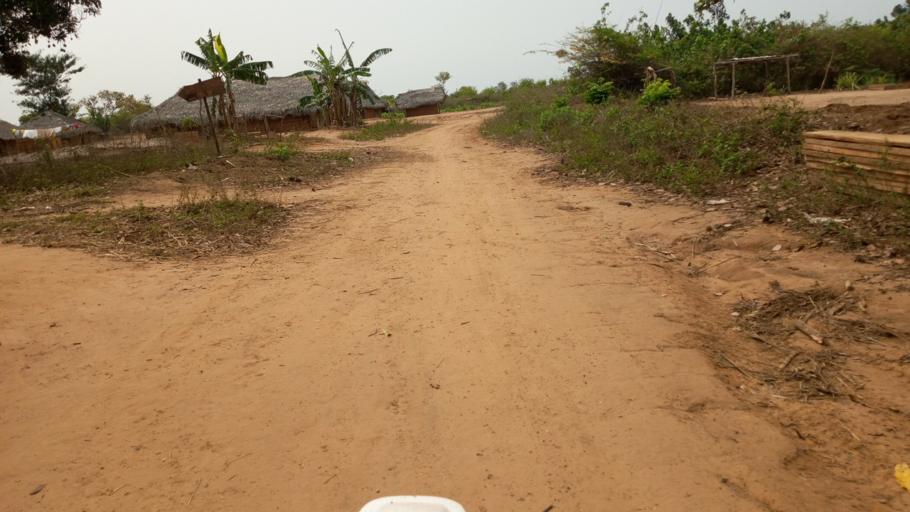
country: CD
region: Bandundu
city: Bandundu
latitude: -3.4518
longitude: 17.7686
